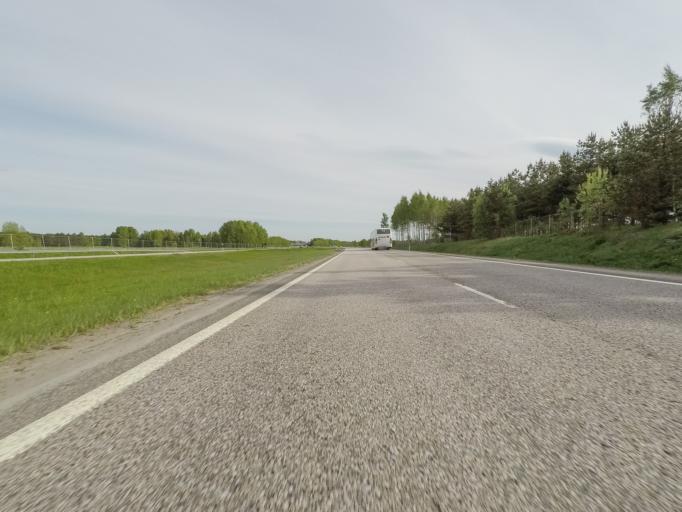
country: FI
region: Uusimaa
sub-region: Helsinki
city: Hyvinge
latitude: 60.5869
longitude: 24.7984
